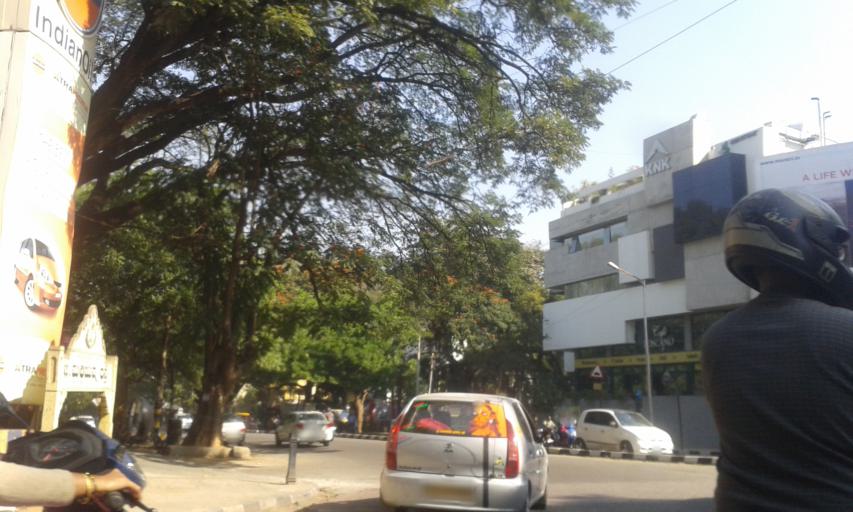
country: IN
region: Karnataka
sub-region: Bangalore Urban
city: Bangalore
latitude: 12.9367
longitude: 77.5850
